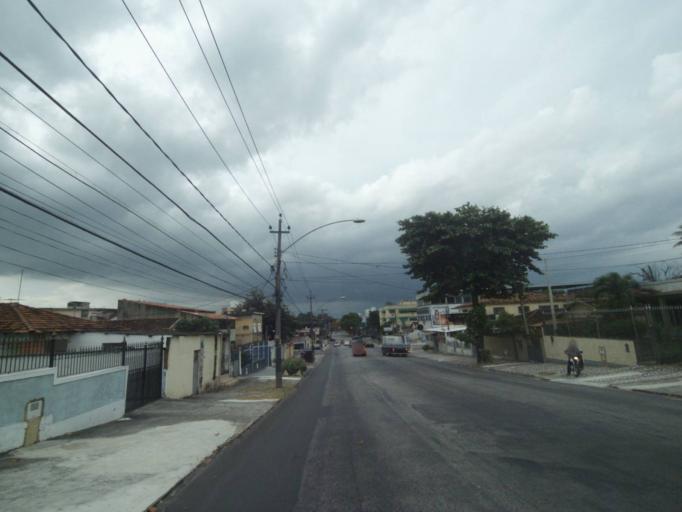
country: BR
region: Rio de Janeiro
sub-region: Nilopolis
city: Nilopolis
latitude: -22.8887
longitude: -43.3905
